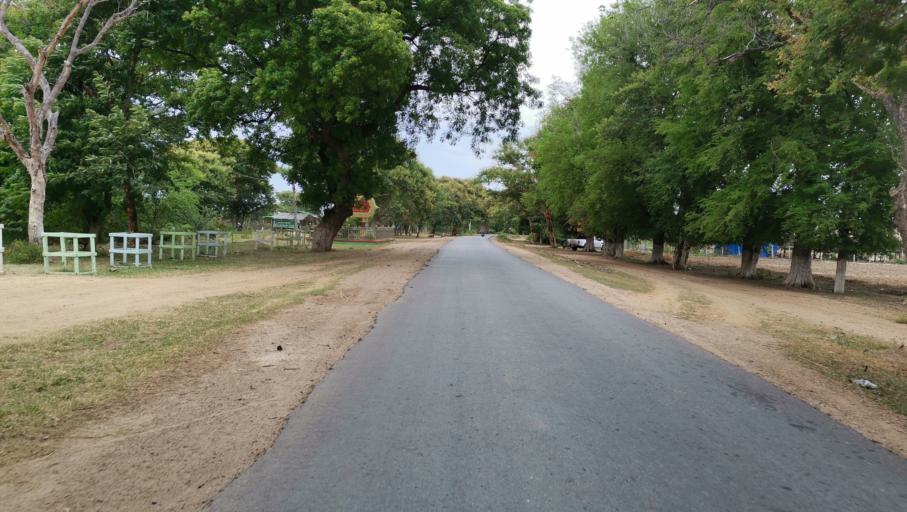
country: MM
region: Mandalay
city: Myingyan
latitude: 21.8488
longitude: 95.4302
